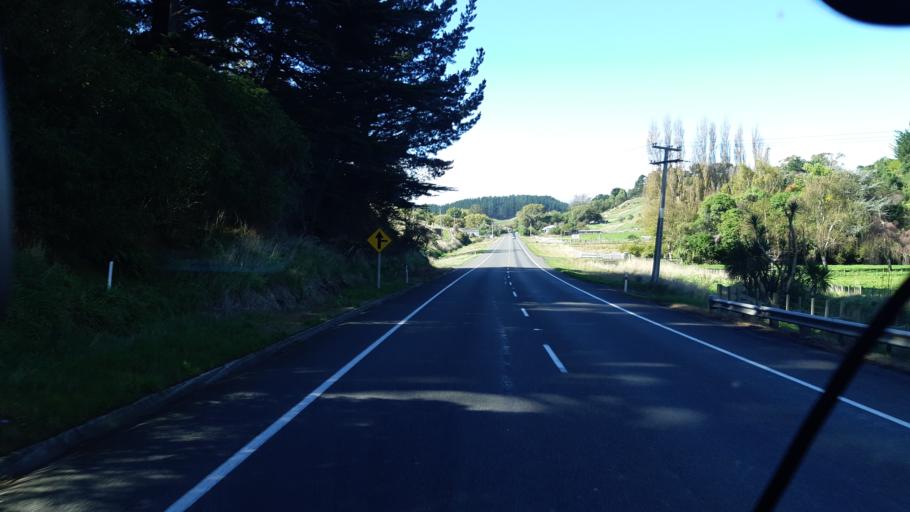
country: NZ
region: Manawatu-Wanganui
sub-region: Wanganui District
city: Wanganui
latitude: -39.9586
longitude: 175.0862
